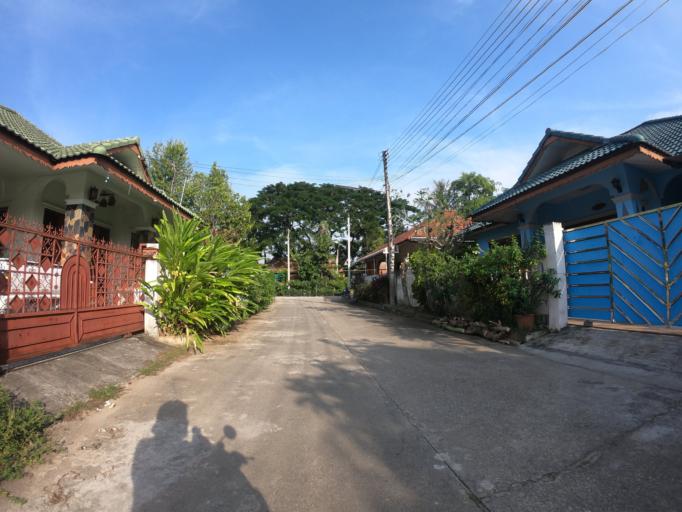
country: TH
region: Chiang Mai
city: Chiang Mai
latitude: 18.8246
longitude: 99.0017
